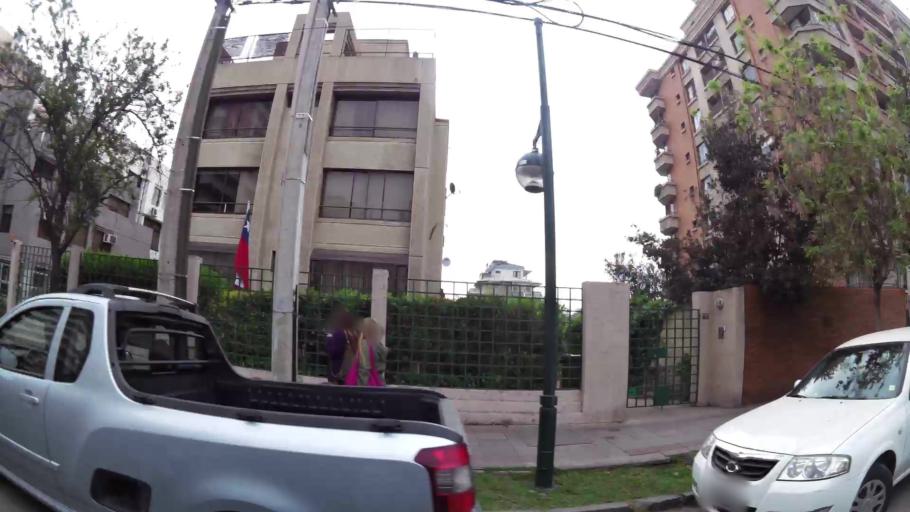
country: CL
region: Santiago Metropolitan
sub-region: Provincia de Santiago
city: Villa Presidente Frei, Nunoa, Santiago, Chile
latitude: -33.4498
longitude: -70.6133
